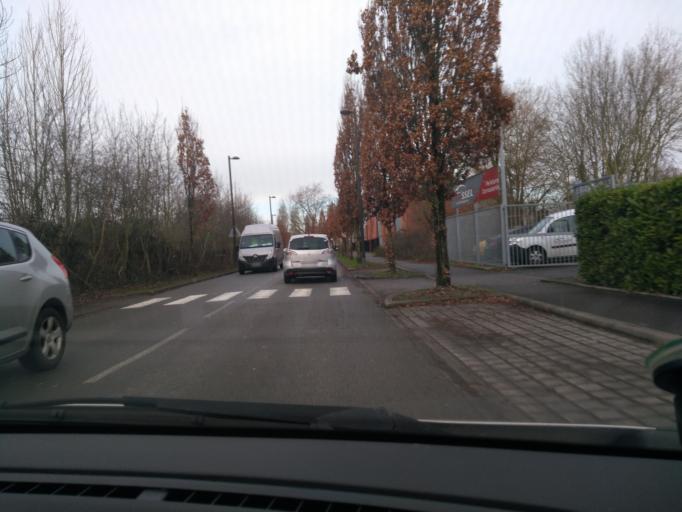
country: FR
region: Nord-Pas-de-Calais
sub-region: Departement du Nord
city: Maubeuge
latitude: 50.2893
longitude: 3.9740
